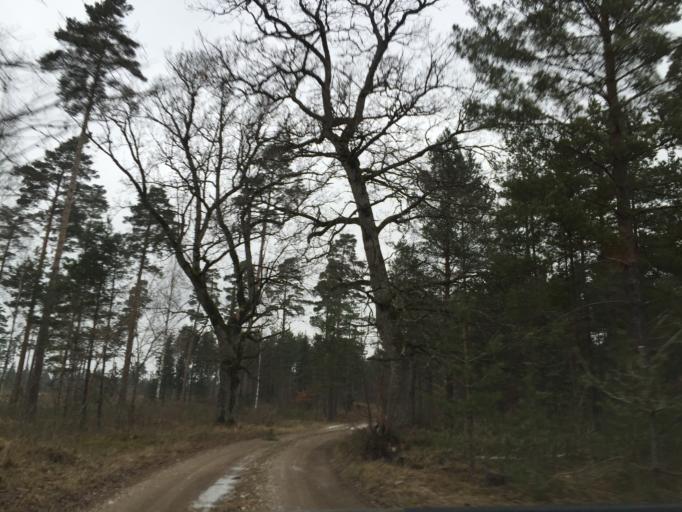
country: EE
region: Saare
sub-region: Kuressaare linn
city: Kuressaare
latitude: 58.3845
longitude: 22.2526
